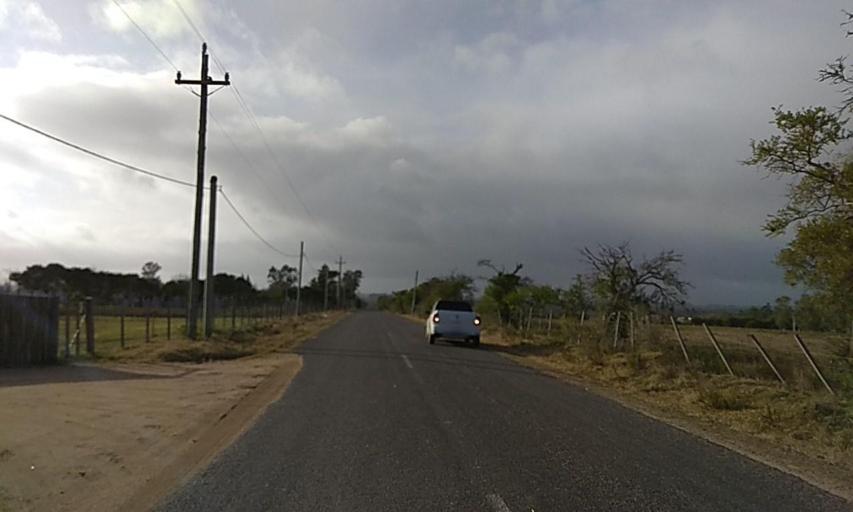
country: UY
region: Florida
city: Florida
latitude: -34.0529
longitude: -56.1985
